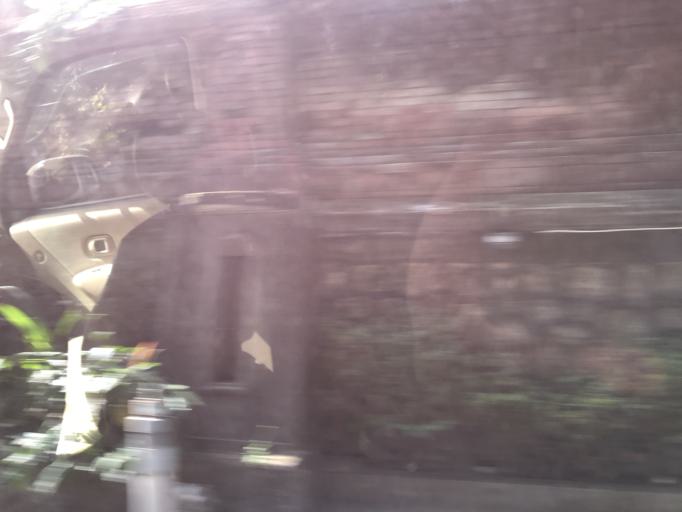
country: ID
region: Bali
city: Banjar Bucu
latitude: -8.5746
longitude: 115.1952
